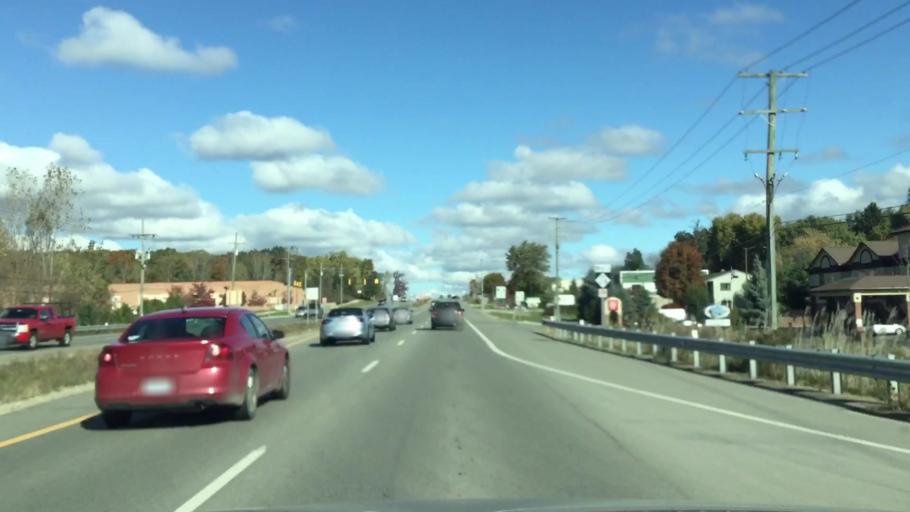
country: US
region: Michigan
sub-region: Oakland County
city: Lake Orion
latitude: 42.7407
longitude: -83.2454
